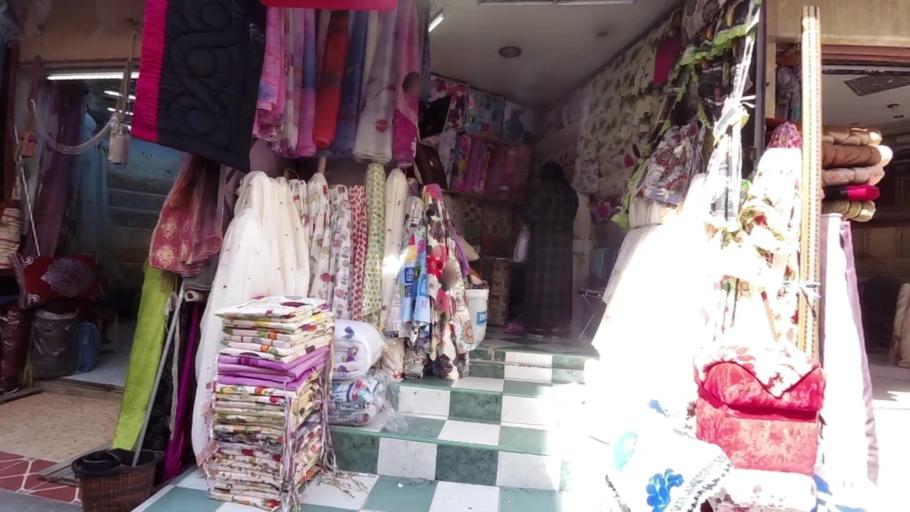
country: MA
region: Tanger-Tetouan
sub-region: Tanger-Assilah
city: Tangier
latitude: 35.7571
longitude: -5.8096
